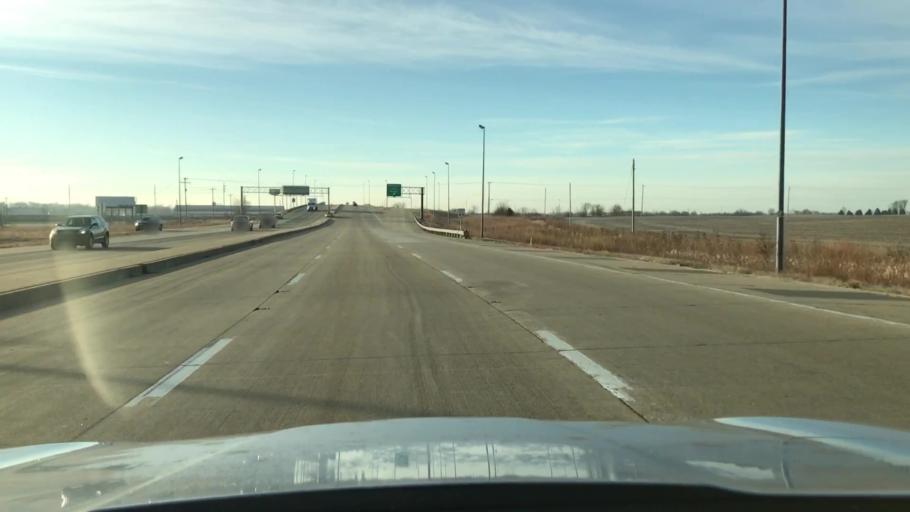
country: US
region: Illinois
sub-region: McLean County
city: Normal
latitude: 40.5347
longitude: -88.9513
